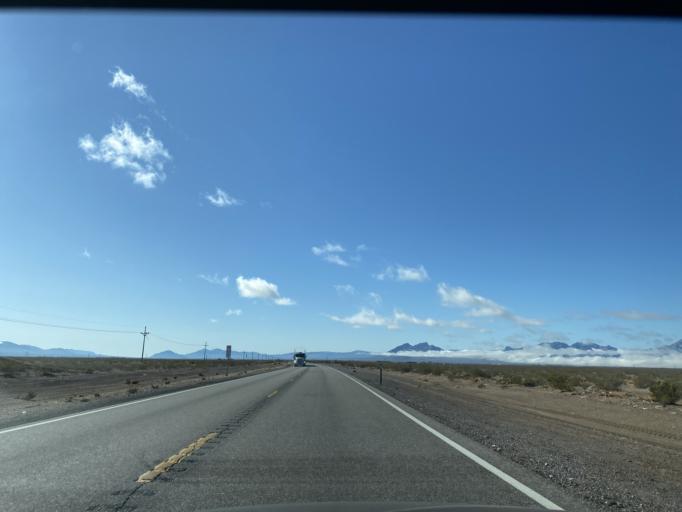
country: US
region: Nevada
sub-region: Nye County
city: Beatty
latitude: 36.5542
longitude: -116.4162
